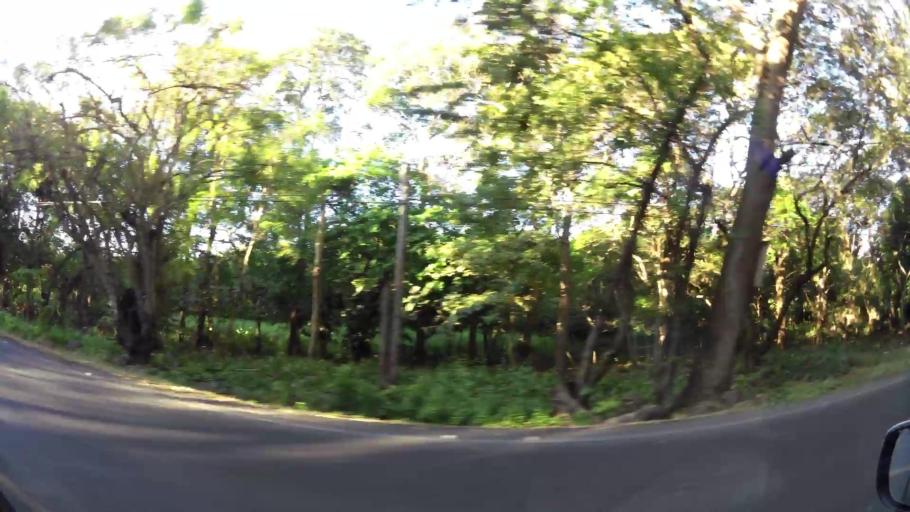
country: CR
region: Puntarenas
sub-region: Canton Central de Puntarenas
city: Chacarita
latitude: 10.0168
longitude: -84.7302
